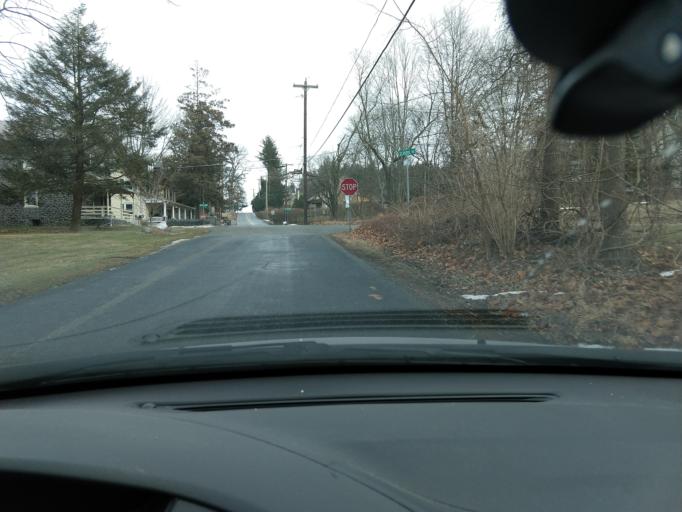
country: US
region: Pennsylvania
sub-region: Montgomery County
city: Stowe
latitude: 40.1893
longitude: -75.7239
